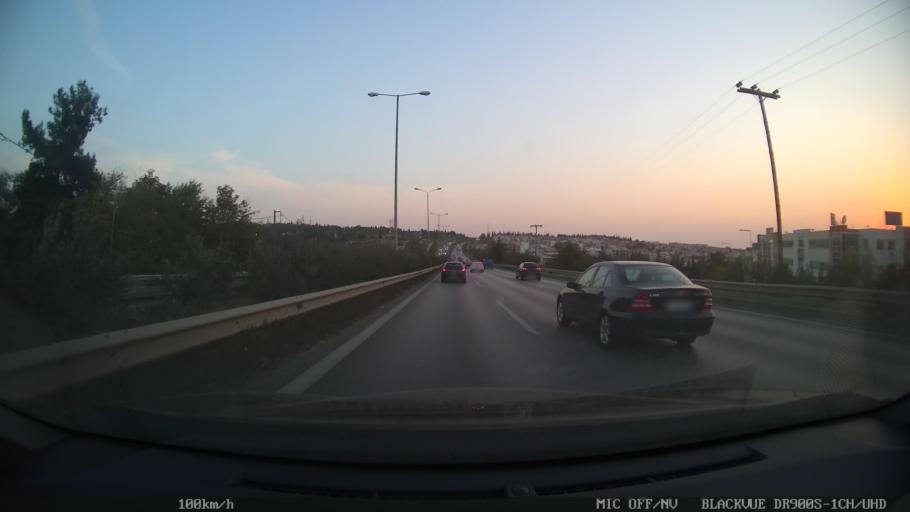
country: GR
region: Central Macedonia
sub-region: Nomos Thessalonikis
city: Pylaia
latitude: 40.6071
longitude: 22.9995
